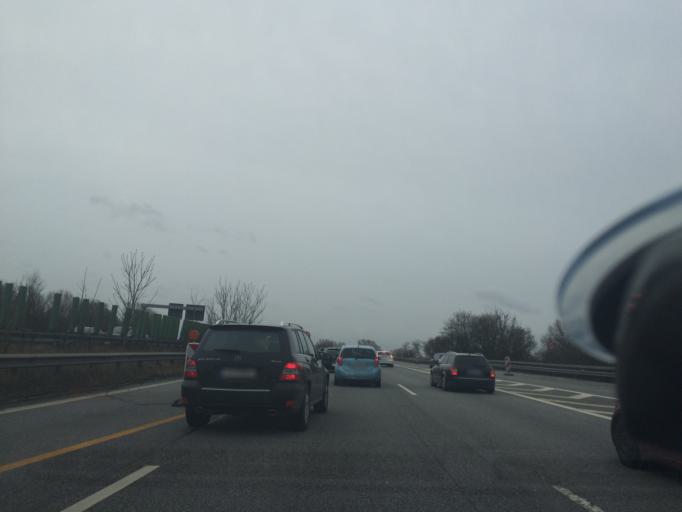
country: DE
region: Hamburg
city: Harburg
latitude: 53.4800
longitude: 10.0227
